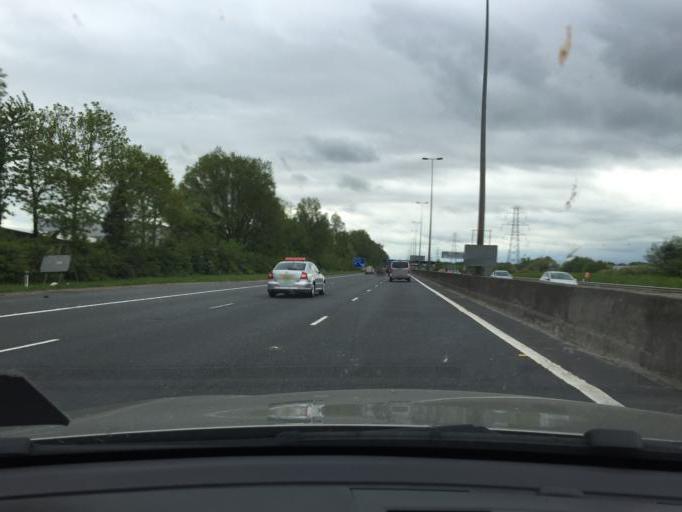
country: GB
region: Northern Ireland
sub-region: City of Belfast
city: Belfast
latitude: 54.5846
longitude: -5.9632
